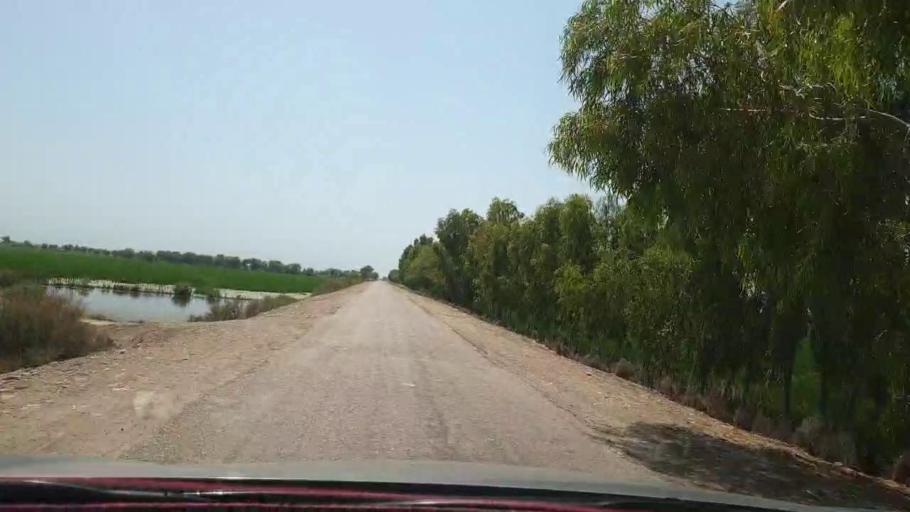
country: PK
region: Sindh
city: Warah
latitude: 27.5407
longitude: 67.7914
